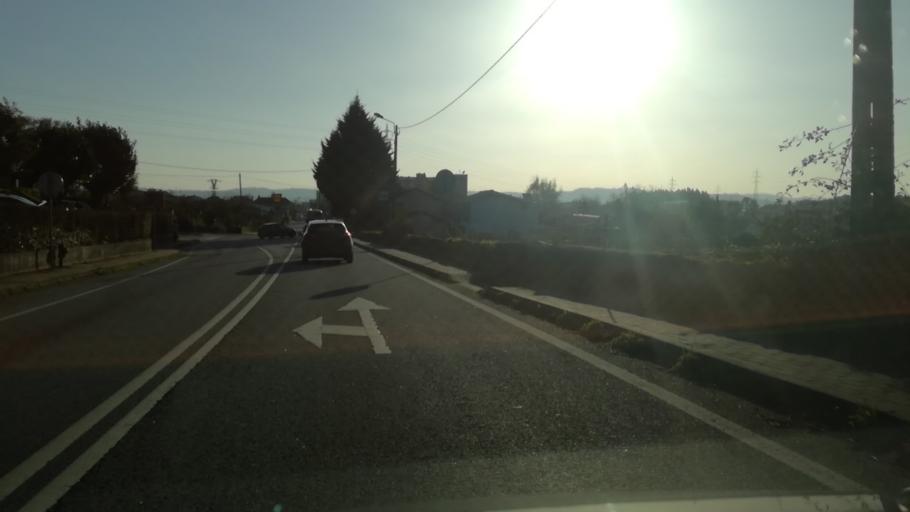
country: PT
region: Braga
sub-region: Vila Nova de Famalicao
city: Ferreiros
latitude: 41.3555
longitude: -8.5527
